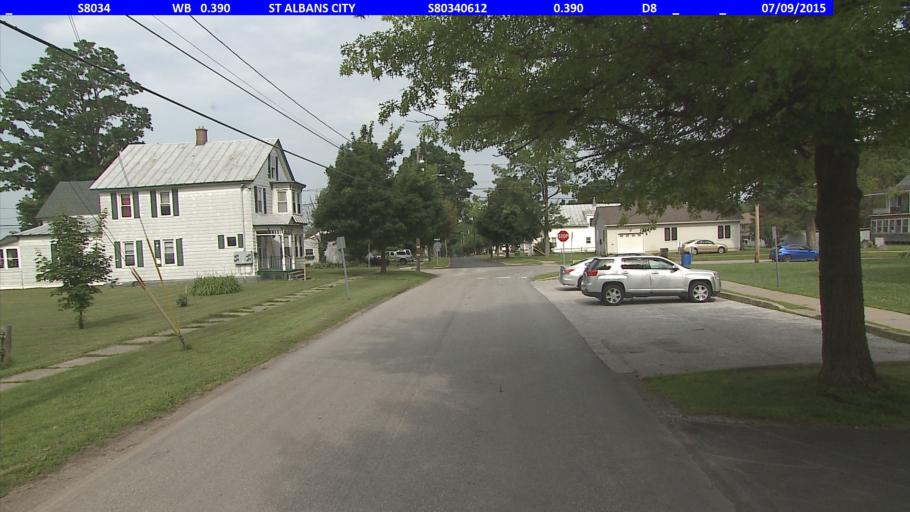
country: US
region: Vermont
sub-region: Franklin County
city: Saint Albans
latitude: 44.8047
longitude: -73.0779
